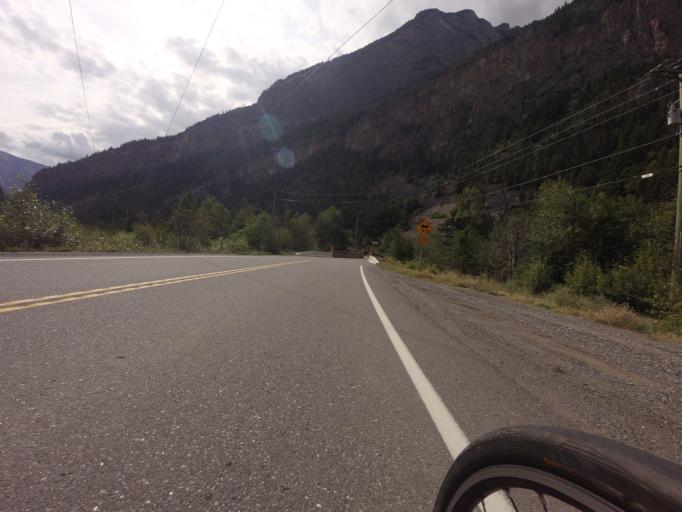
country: CA
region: British Columbia
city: Lillooet
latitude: 50.6693
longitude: -121.9659
